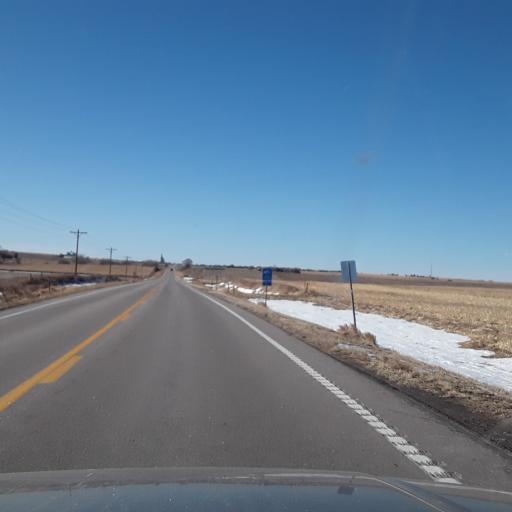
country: US
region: Nebraska
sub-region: Dawson County
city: Gothenburg
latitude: 40.7040
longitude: -100.1702
